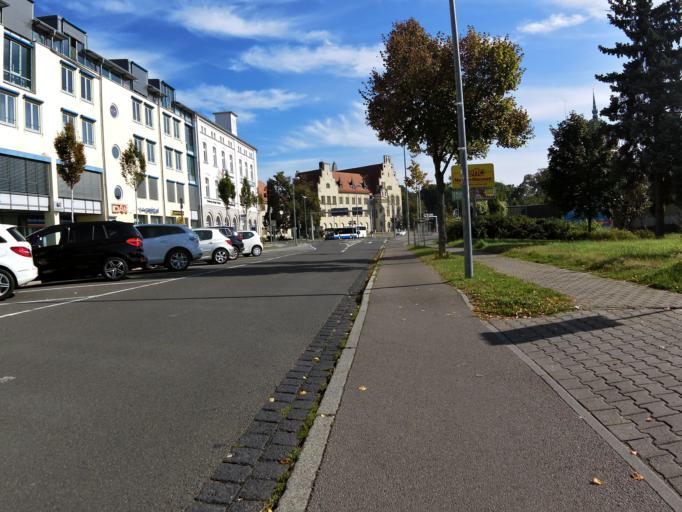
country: DE
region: Saxony-Anhalt
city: Wittenburg
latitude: 51.8665
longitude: 12.6328
